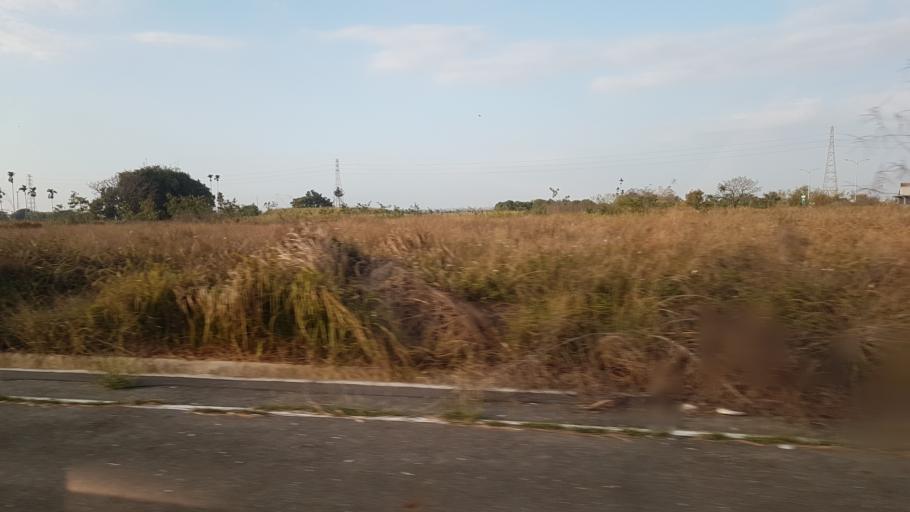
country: TW
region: Taiwan
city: Xinying
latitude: 23.3501
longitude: 120.3784
